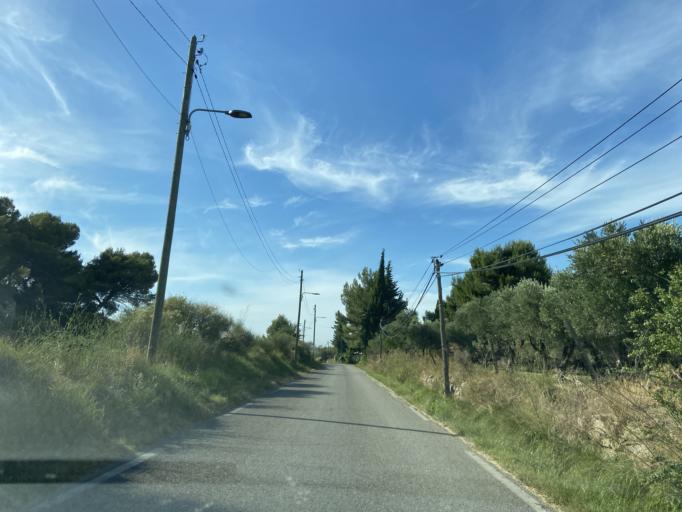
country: FR
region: Provence-Alpes-Cote d'Azur
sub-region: Departement des Bouches-du-Rhone
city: Saint-Chamas
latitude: 43.5655
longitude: 5.0207
